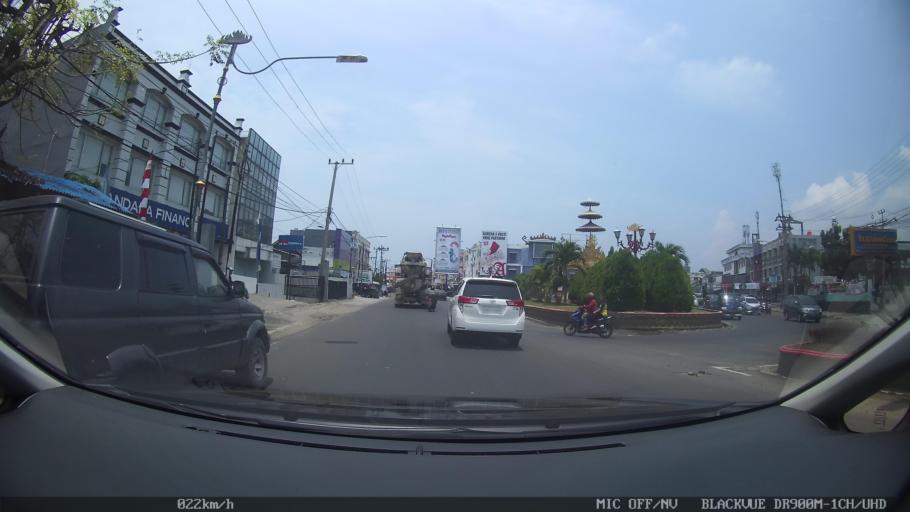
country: ID
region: Lampung
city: Bandarlampung
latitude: -5.4397
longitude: 105.2657
